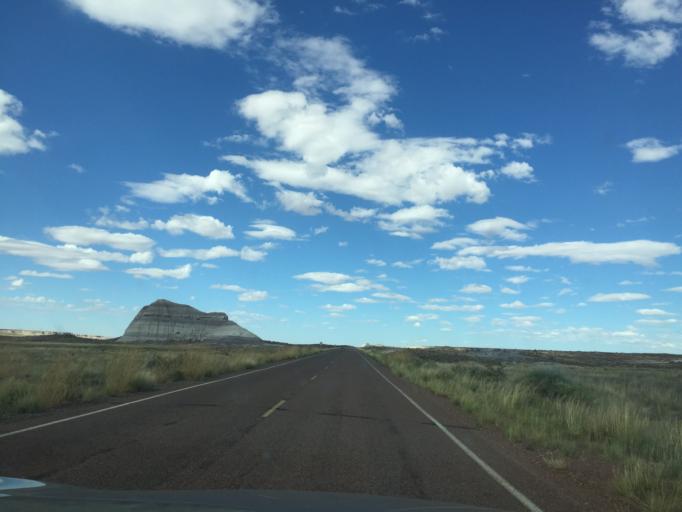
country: US
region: Arizona
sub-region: Navajo County
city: Holbrook
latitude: 34.8598
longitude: -109.7942
